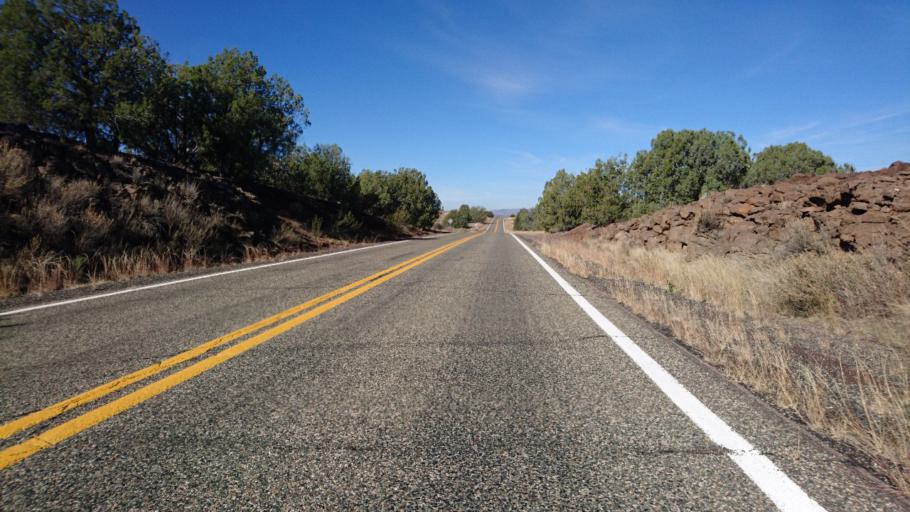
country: US
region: Arizona
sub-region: Yavapai County
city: Paulden
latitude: 35.2805
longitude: -112.7053
